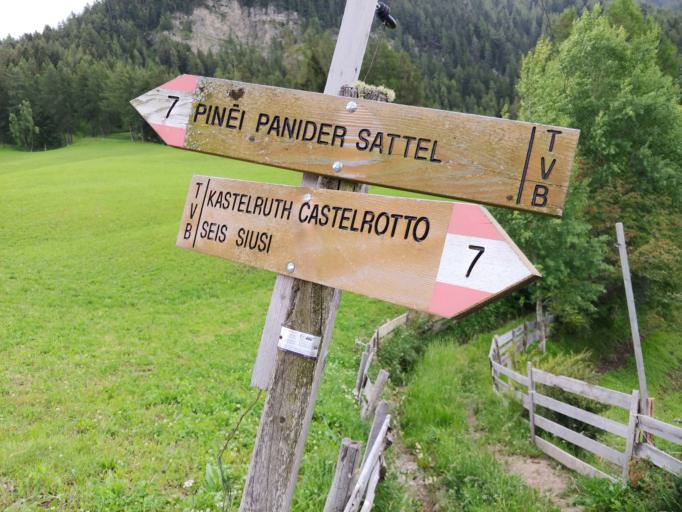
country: IT
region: Trentino-Alto Adige
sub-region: Bolzano
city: Castelrotto
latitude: 46.5776
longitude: 11.6137
